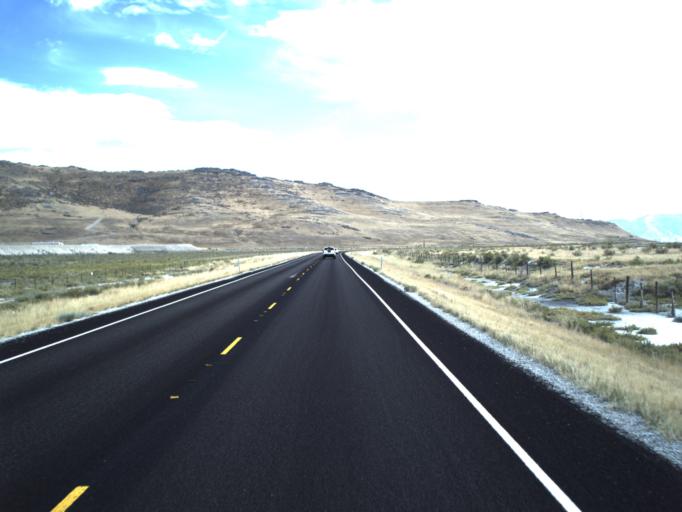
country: US
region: Utah
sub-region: Box Elder County
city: Tremonton
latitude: 41.6279
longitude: -112.4043
